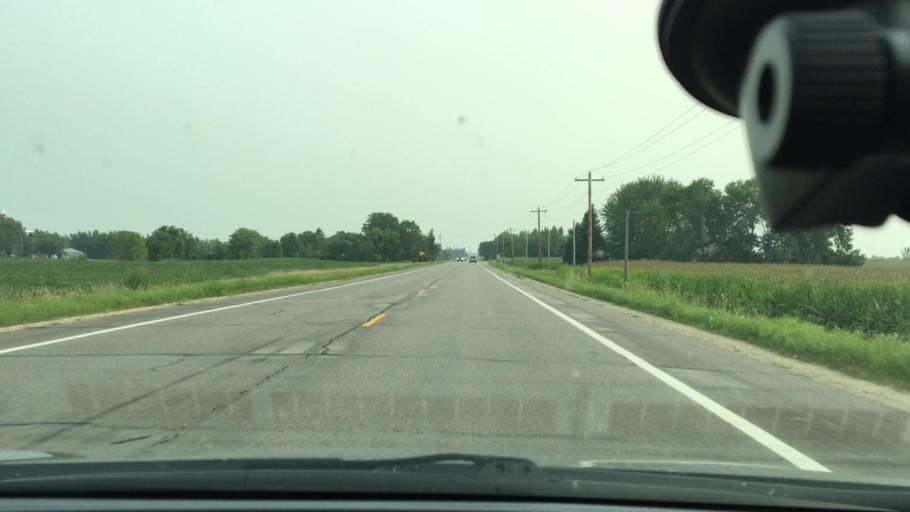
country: US
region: Minnesota
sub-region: Wright County
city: Albertville
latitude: 45.2700
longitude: -93.6636
